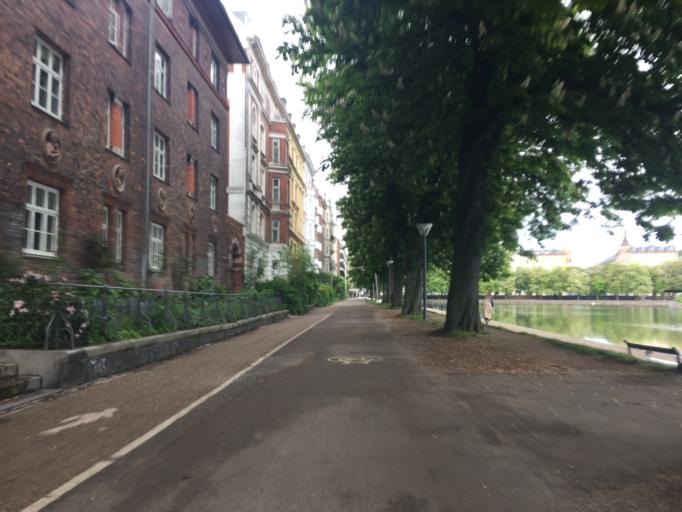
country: DK
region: Capital Region
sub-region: Kobenhavn
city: Copenhagen
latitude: 55.6964
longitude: 12.5754
